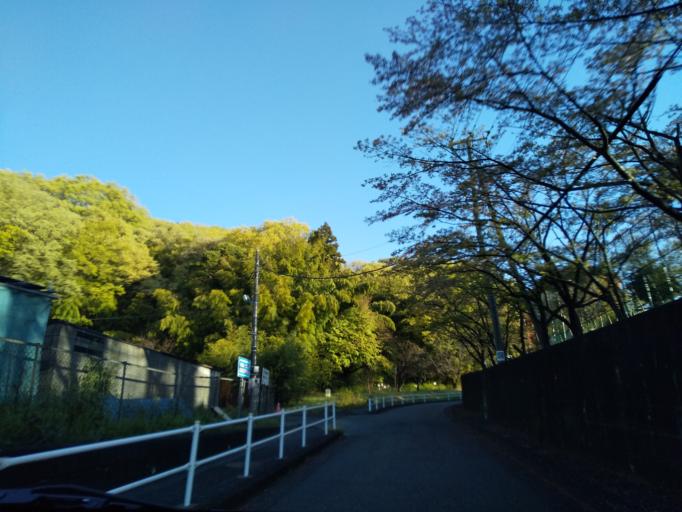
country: JP
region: Tokyo
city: Hachioji
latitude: 35.6221
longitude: 139.3605
